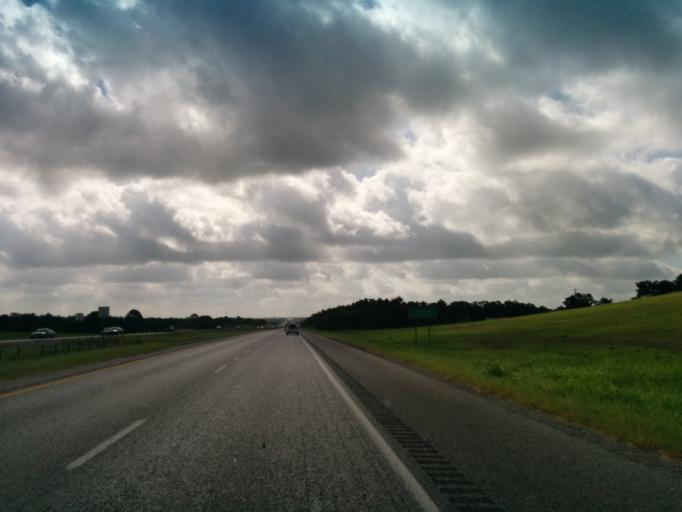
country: US
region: Texas
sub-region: Caldwell County
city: Luling
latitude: 29.6533
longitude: -97.5561
